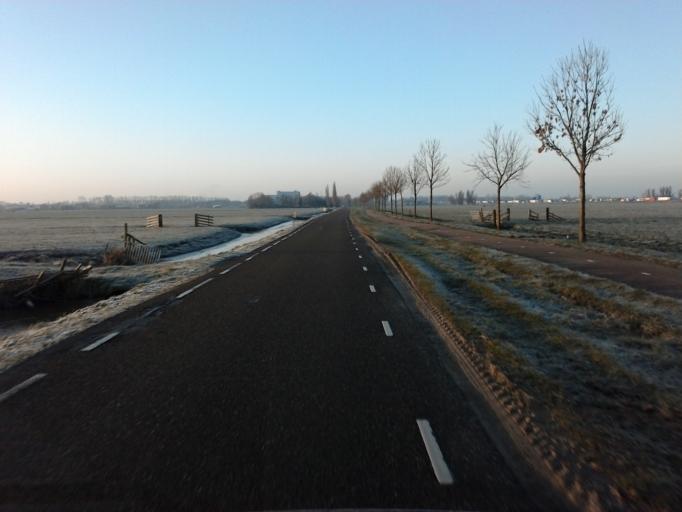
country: NL
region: South Holland
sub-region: Gemeente Gorinchem
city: Gorinchem
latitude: 51.8590
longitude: 4.9630
